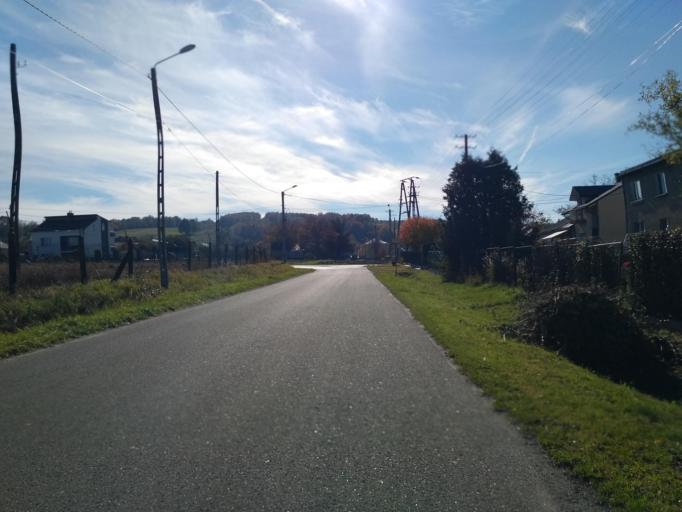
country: PL
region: Subcarpathian Voivodeship
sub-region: Powiat ropczycko-sedziszowski
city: Iwierzyce
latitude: 50.0583
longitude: 21.7862
